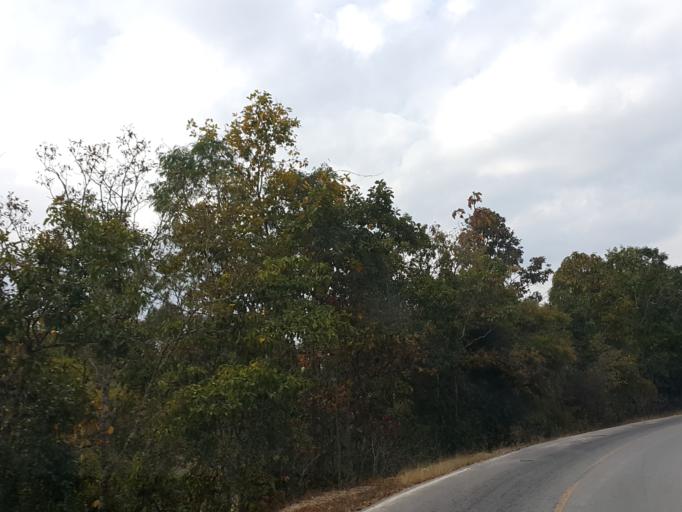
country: TH
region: Chiang Mai
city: Om Koi
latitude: 17.7985
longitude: 98.3416
